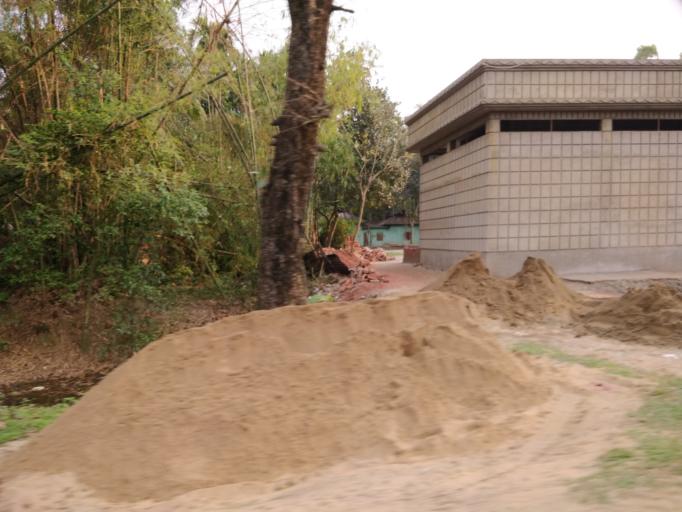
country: IN
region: Tripura
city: Khowai
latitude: 24.1310
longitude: 91.3576
